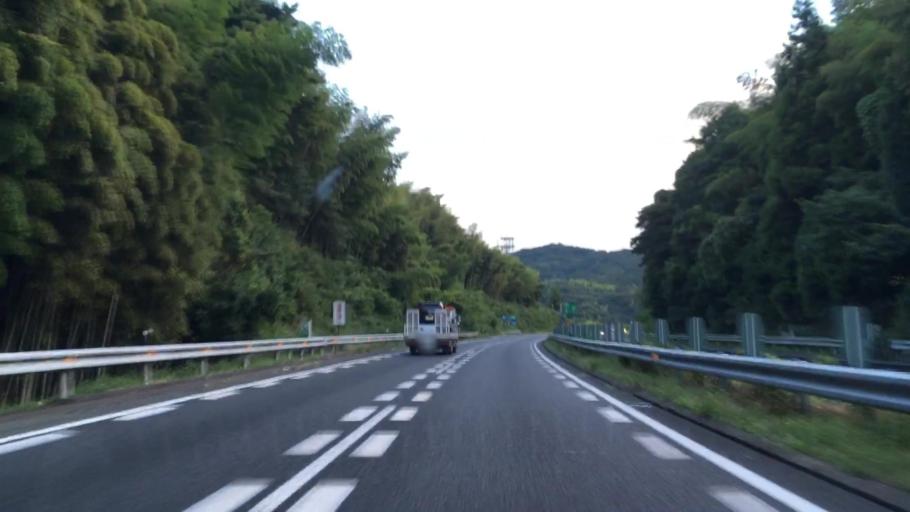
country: JP
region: Yamaguchi
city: Shimonoseki
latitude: 33.9341
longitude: 130.9961
